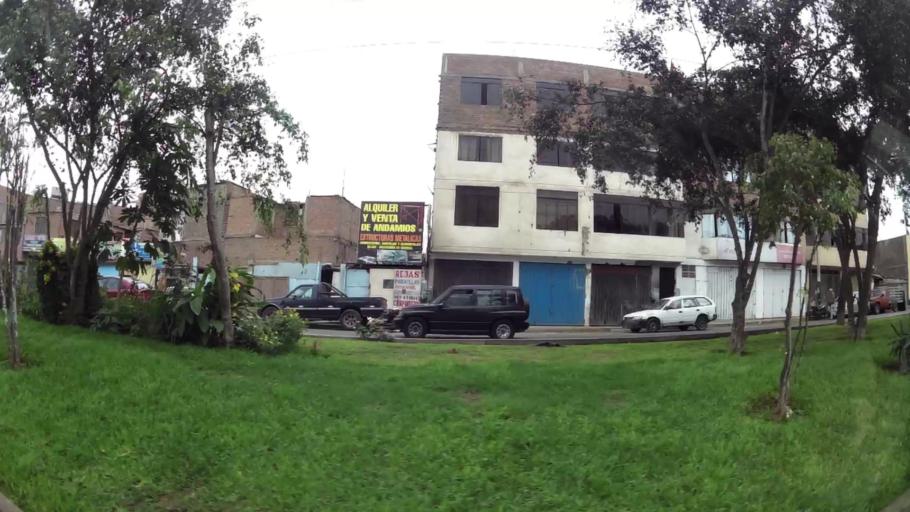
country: PE
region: Lima
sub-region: Lima
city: Surco
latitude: -12.1189
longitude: -76.9972
